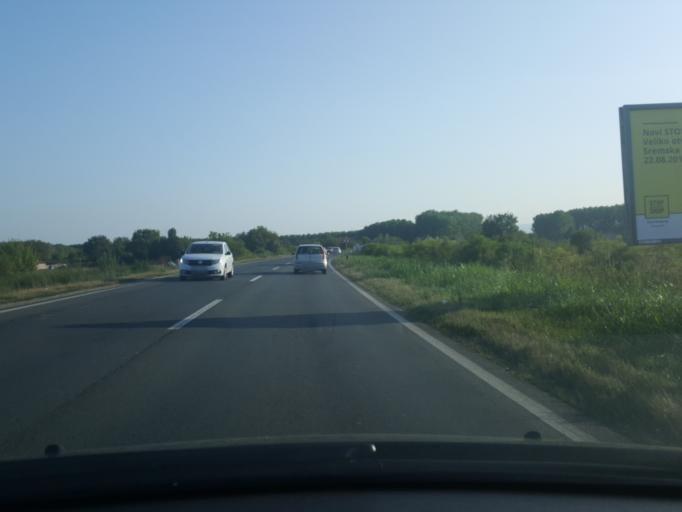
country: RS
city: Klenak
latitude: 44.7651
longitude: 19.7247
